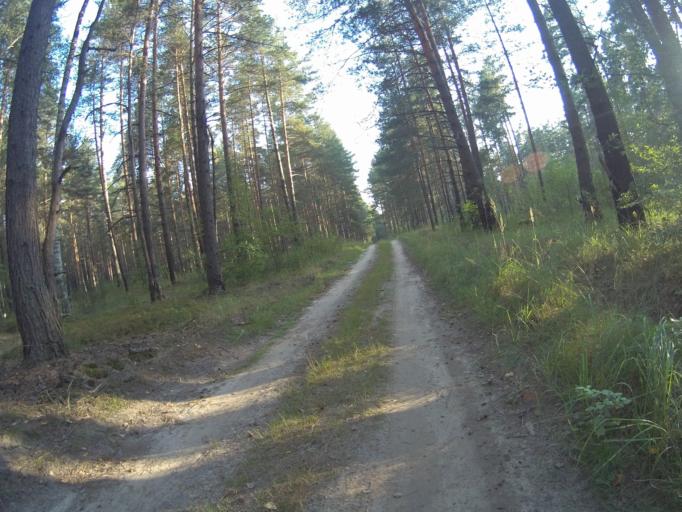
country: RU
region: Vladimir
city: Raduzhnyy
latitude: 55.9885
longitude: 40.2878
